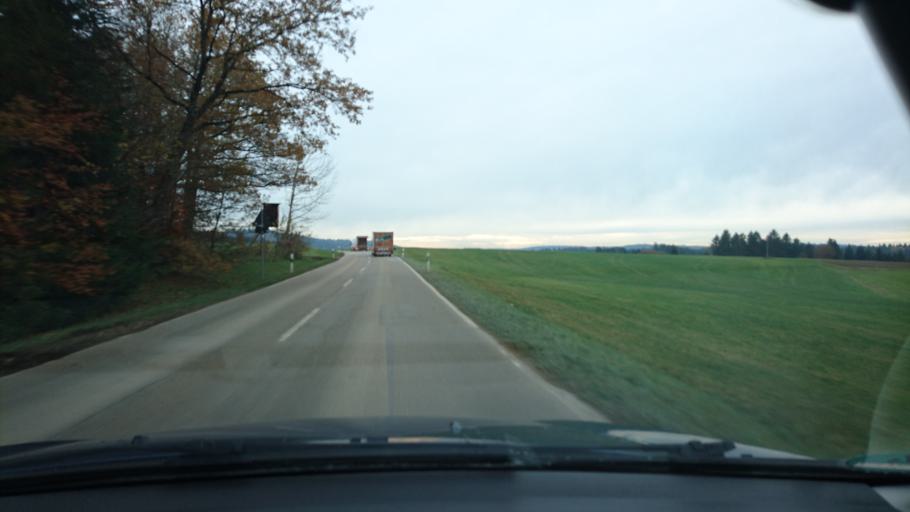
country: DE
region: Baden-Wuerttemberg
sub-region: Regierungsbezirk Stuttgart
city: Gschwend
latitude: 48.9233
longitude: 9.7060
